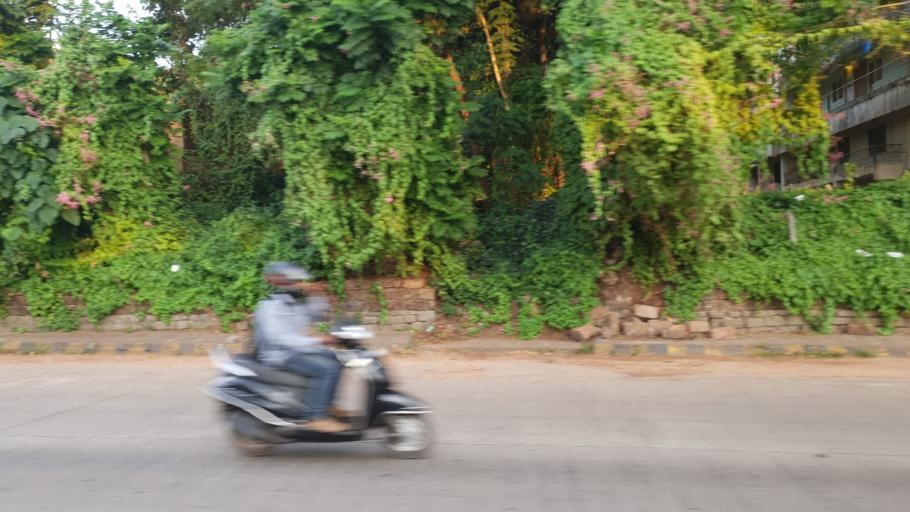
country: IN
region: Karnataka
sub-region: Dakshina Kannada
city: Mangalore
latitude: 12.8928
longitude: 74.8358
